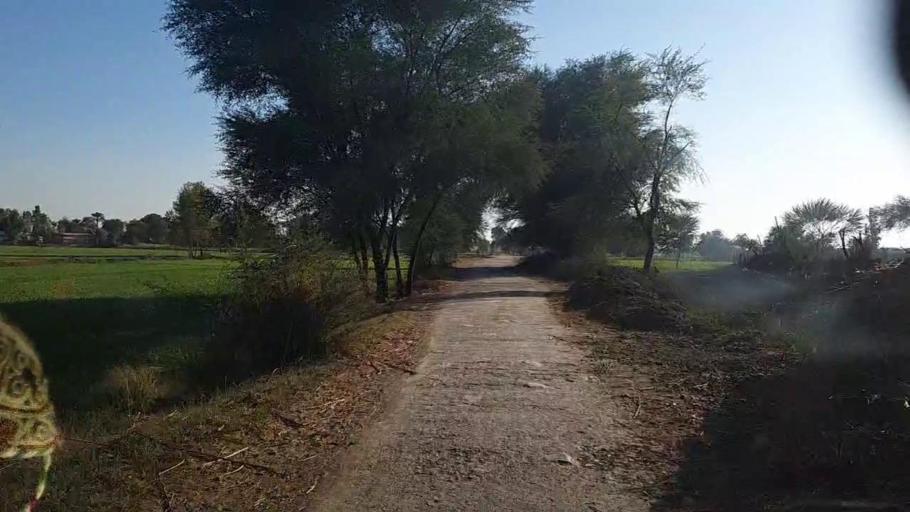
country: PK
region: Sindh
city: Khairpur
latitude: 28.0028
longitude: 69.7196
